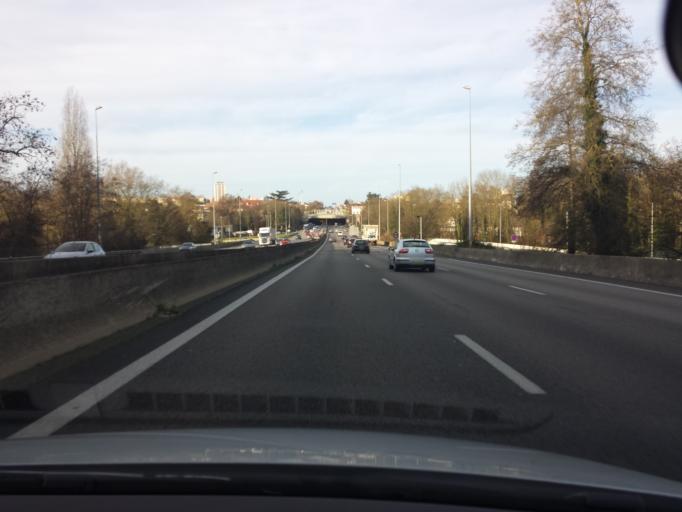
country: FR
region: Ile-de-France
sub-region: Departement des Yvelines
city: Mantes-la-Jolie
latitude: 48.9763
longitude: 1.7206
